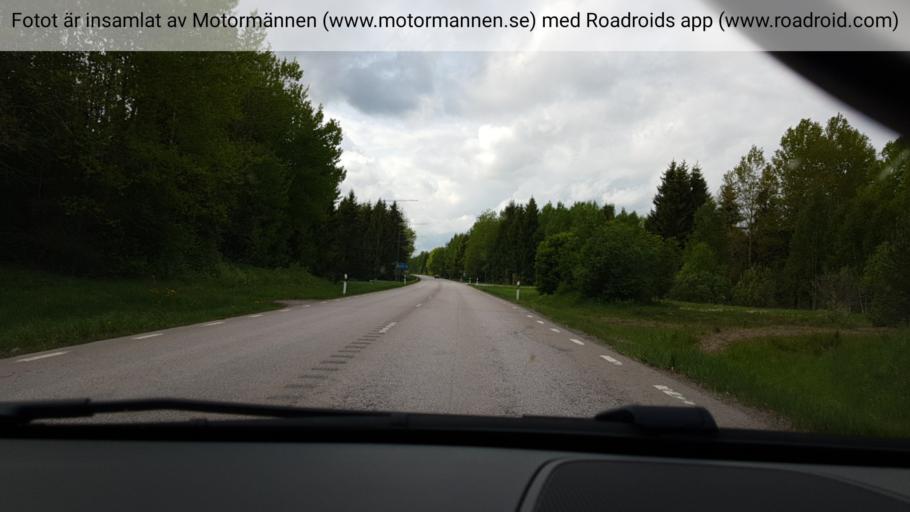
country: SE
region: Uppsala
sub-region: Tierps Kommun
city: Orbyhus
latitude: 60.2567
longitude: 17.6335
